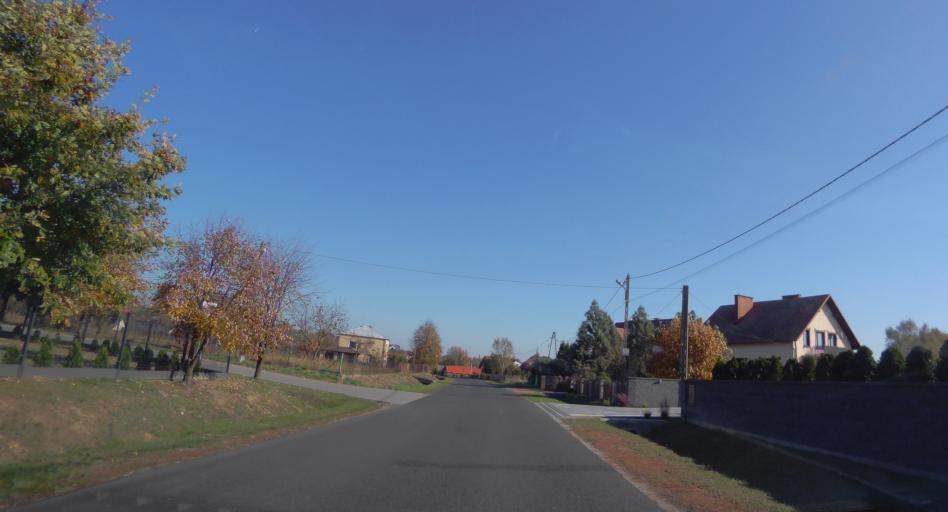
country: PL
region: Subcarpathian Voivodeship
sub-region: Powiat lezajski
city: Wola Zarczycka
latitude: 50.2763
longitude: 22.2634
